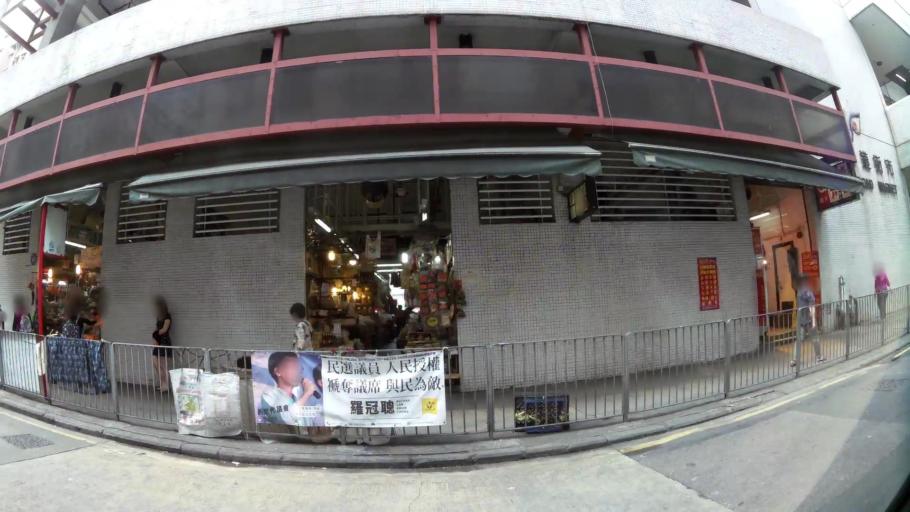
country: HK
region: Wanchai
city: Wan Chai
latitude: 22.2922
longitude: 114.1984
